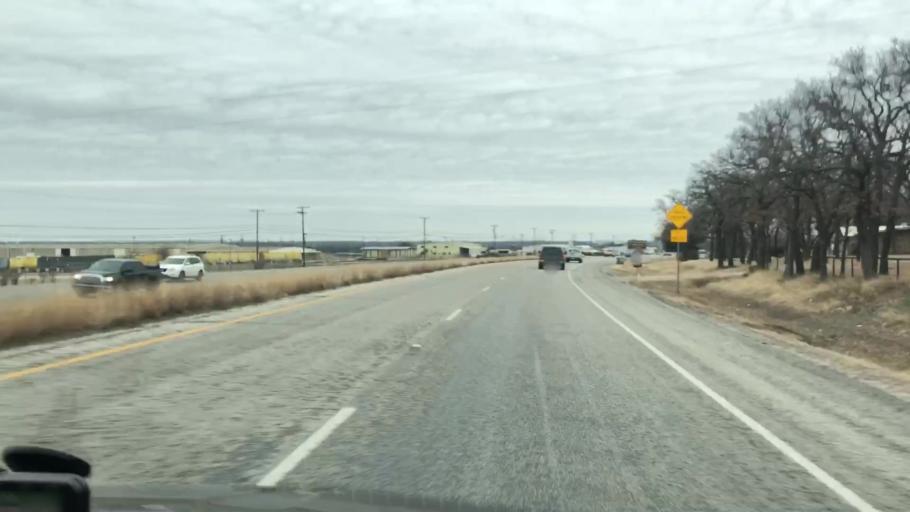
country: US
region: Texas
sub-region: Jack County
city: Jacksboro
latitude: 33.1954
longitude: -98.1449
